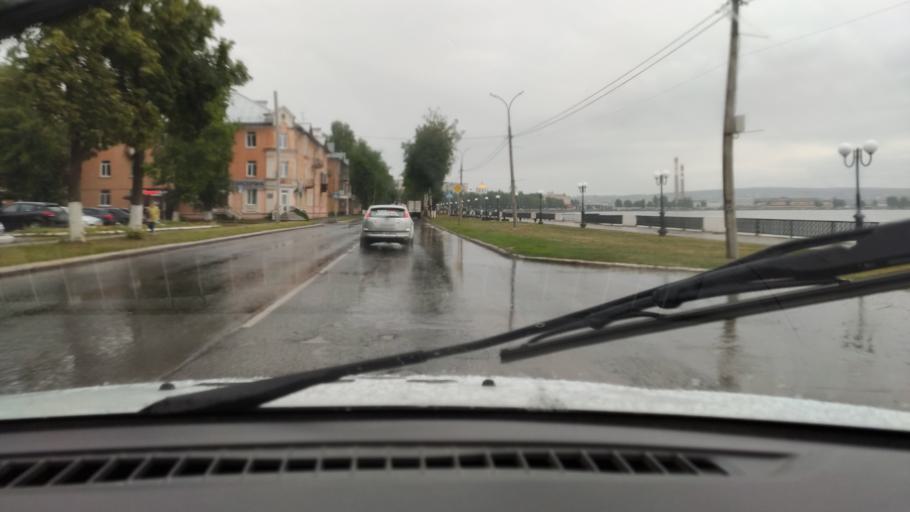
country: RU
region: Udmurtiya
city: Votkinsk
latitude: 57.0595
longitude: 53.9873
